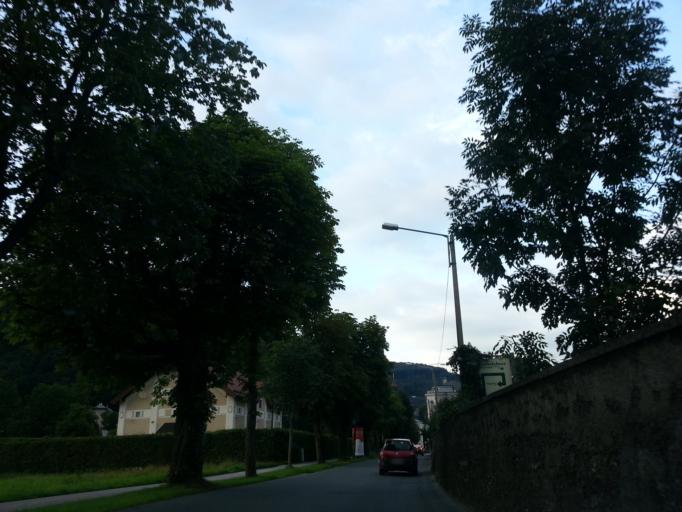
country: AT
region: Salzburg
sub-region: Salzburg Stadt
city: Salzburg
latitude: 47.7909
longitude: 13.0474
